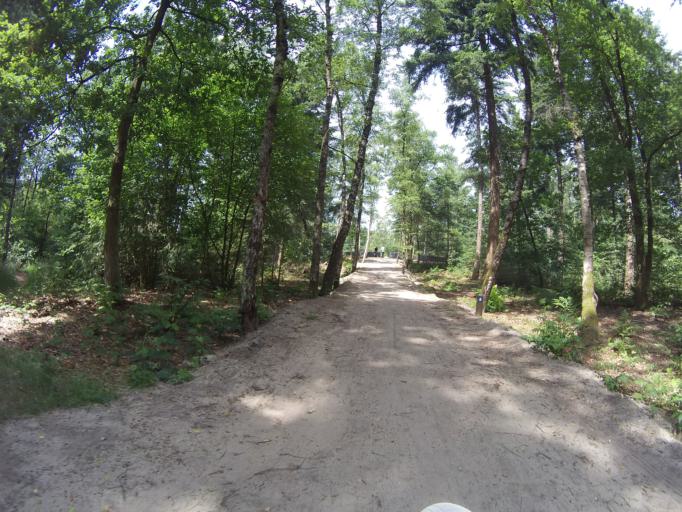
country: NL
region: Gelderland
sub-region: Gemeente Ede
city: Lunteren
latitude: 52.1004
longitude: 5.6465
